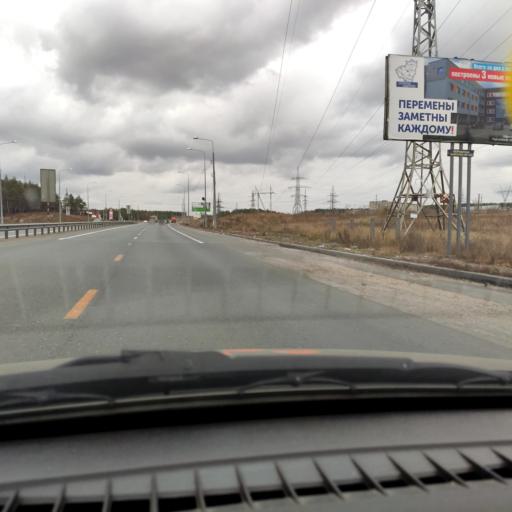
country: RU
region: Samara
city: Zhigulevsk
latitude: 53.4888
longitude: 49.5200
